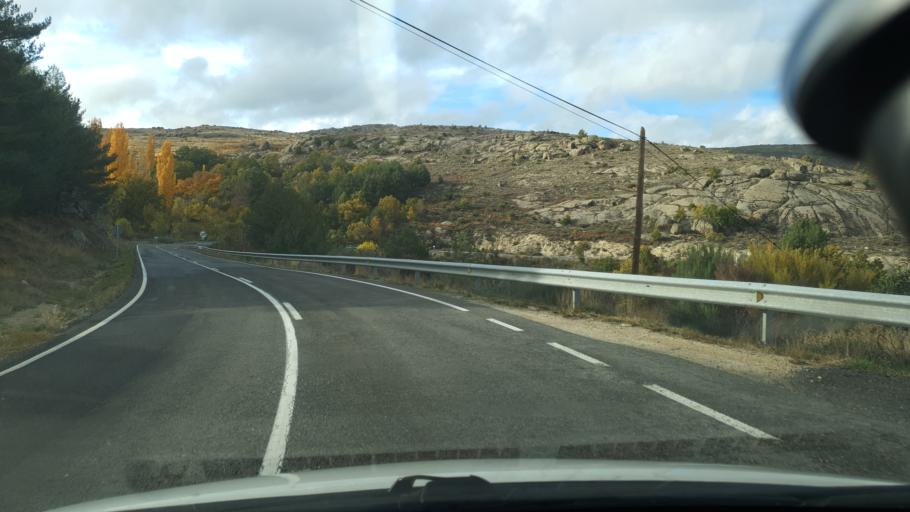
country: ES
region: Castille and Leon
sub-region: Provincia de Avila
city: Navalosa
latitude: 40.3939
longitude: -4.9425
